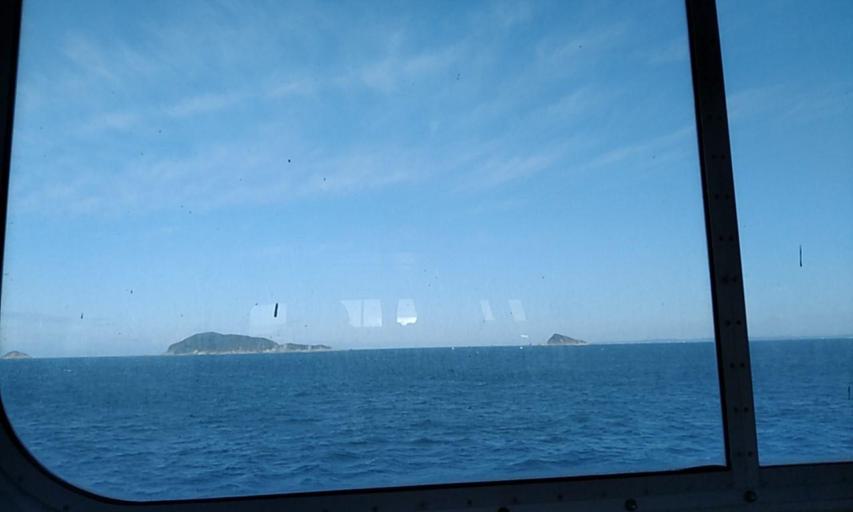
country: JP
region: Mie
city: Toba
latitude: 34.5244
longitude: 136.9349
